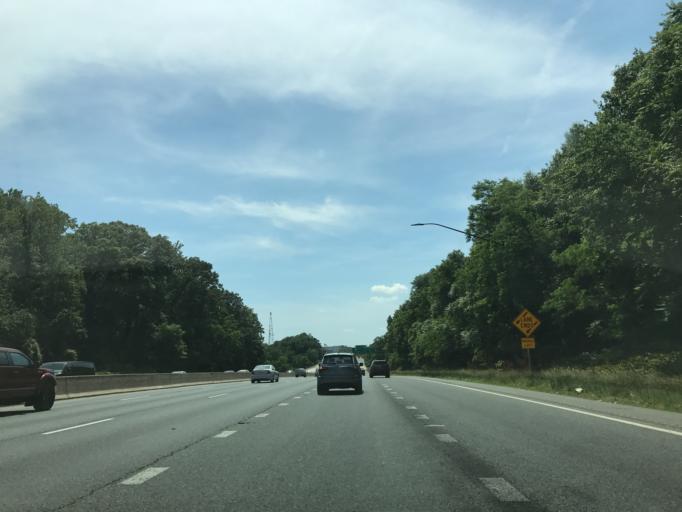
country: US
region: Maryland
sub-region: Anne Arundel County
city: Parole
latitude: 38.9919
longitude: -76.5212
